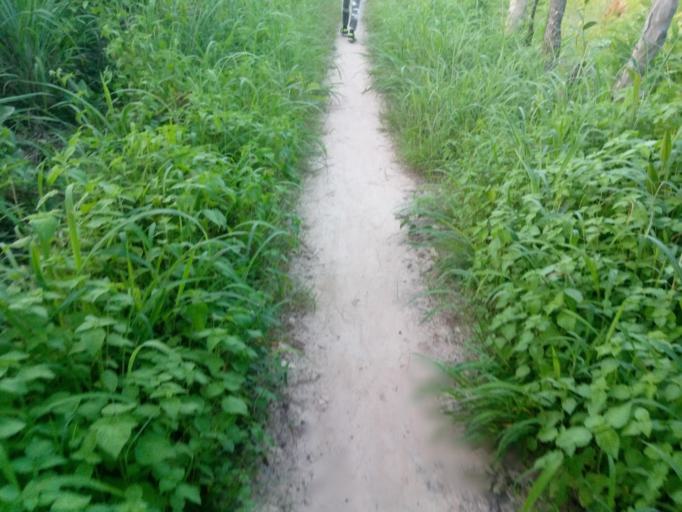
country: GM
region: Western
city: Gunjur
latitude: 13.0372
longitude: -16.7254
